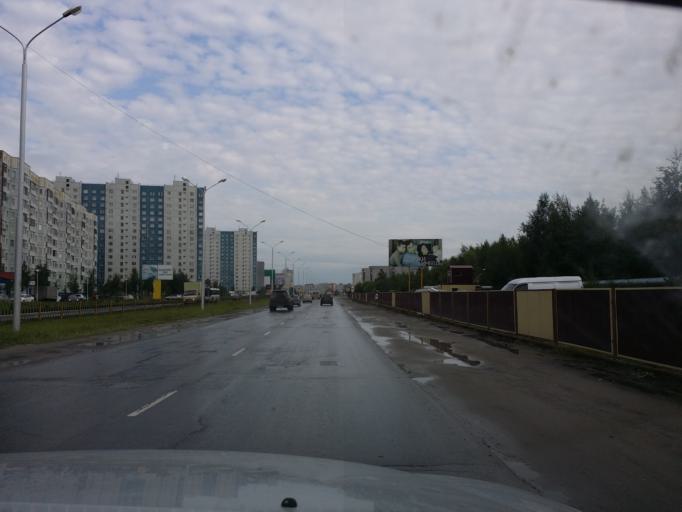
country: RU
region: Khanty-Mansiyskiy Avtonomnyy Okrug
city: Nizhnevartovsk
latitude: 60.9534
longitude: 76.5791
